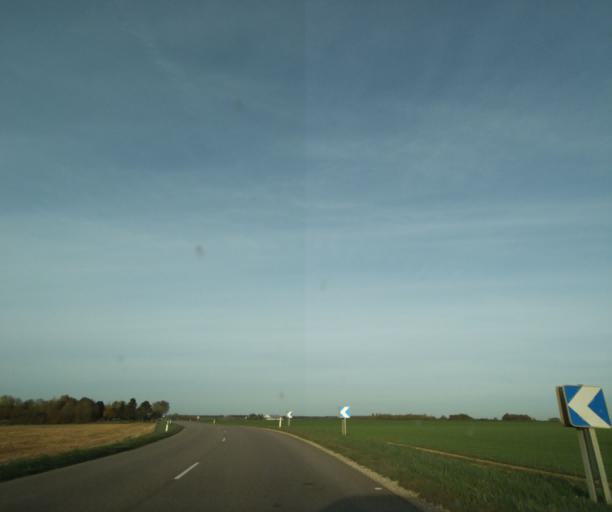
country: FR
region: Lorraine
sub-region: Departement de la Meuse
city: Etain
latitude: 49.2275
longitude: 5.6569
